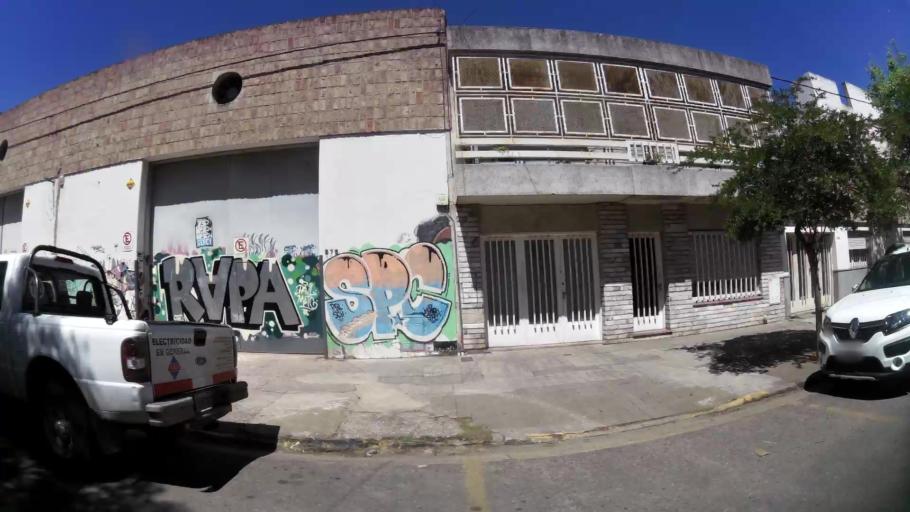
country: AR
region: Santa Fe
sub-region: Departamento de Rosario
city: Rosario
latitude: -32.9394
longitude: -60.6621
